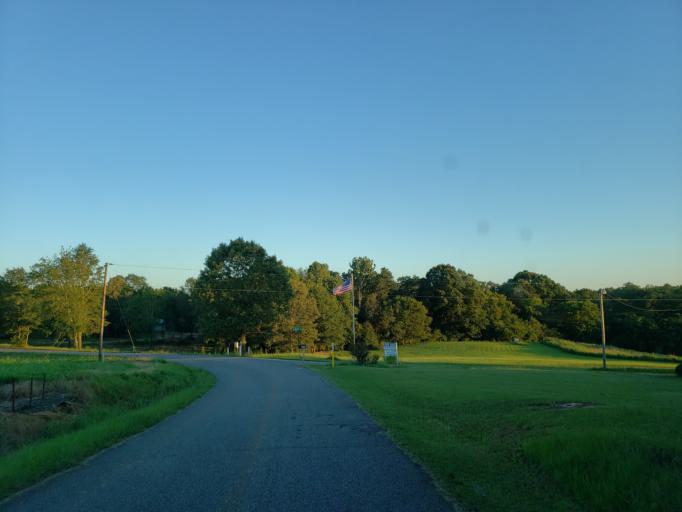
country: US
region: Georgia
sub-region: Bartow County
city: Euharlee
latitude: 34.1051
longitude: -84.8809
